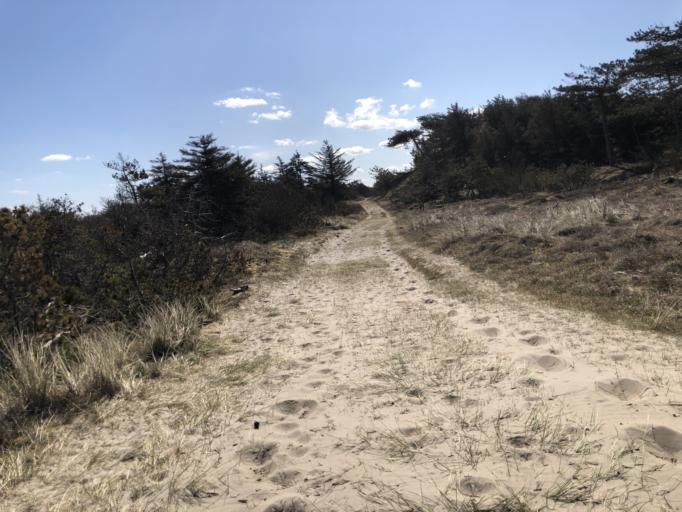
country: DK
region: Central Jutland
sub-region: Holstebro Kommune
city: Ulfborg
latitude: 56.3046
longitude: 8.1312
